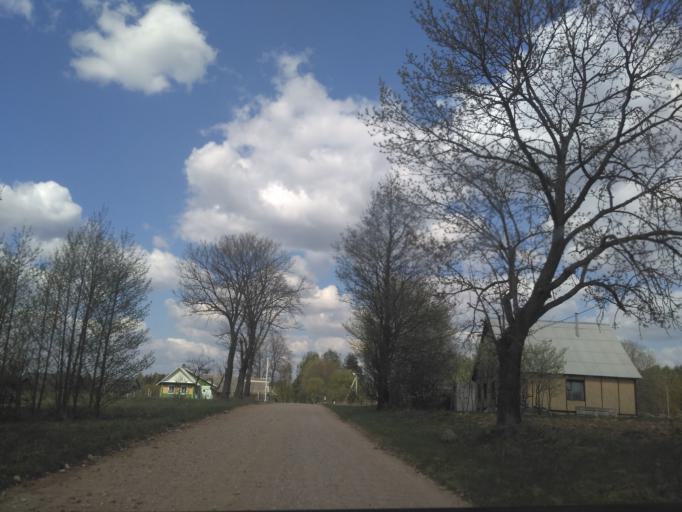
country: BY
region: Minsk
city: Il'ya
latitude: 54.2818
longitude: 27.3008
